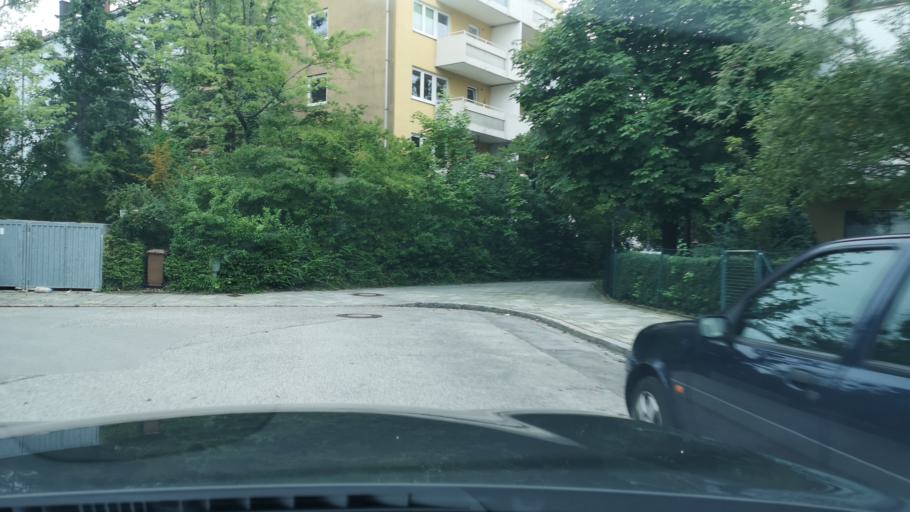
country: DE
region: Bavaria
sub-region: Upper Bavaria
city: Pasing
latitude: 48.1284
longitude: 11.5132
